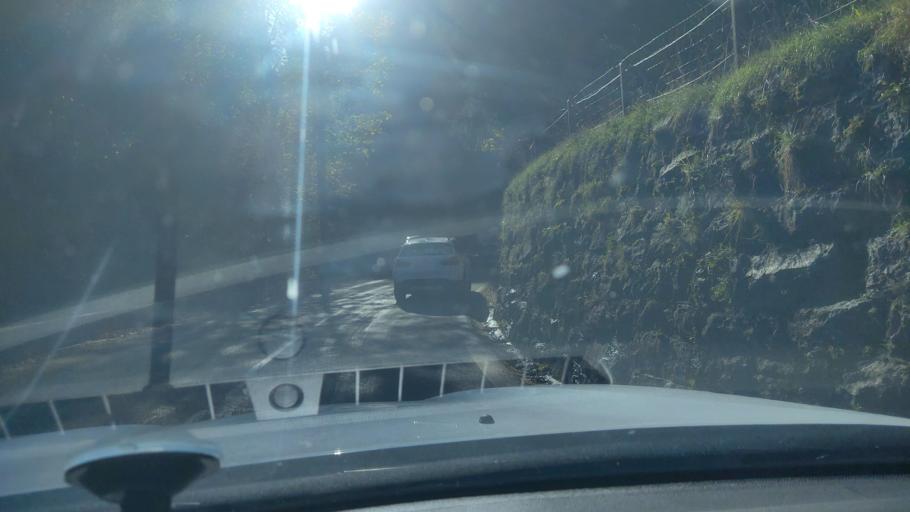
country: FR
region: Rhone-Alpes
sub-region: Departement de la Savoie
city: Ugine
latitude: 45.7846
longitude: 6.4815
